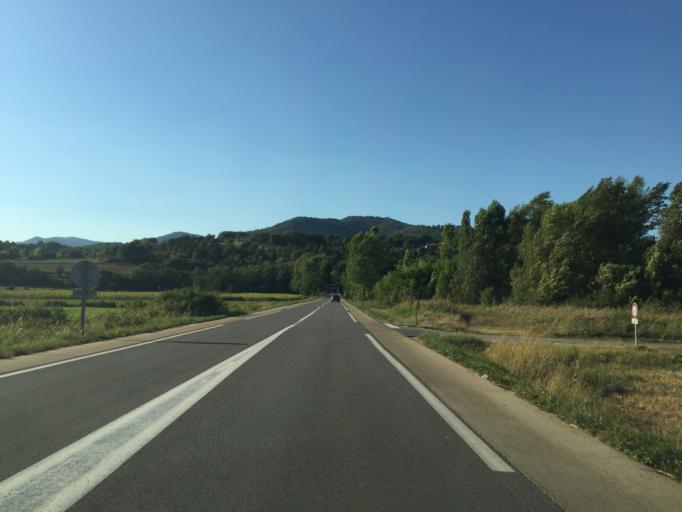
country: FR
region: Provence-Alpes-Cote d'Azur
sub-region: Departement des Alpes-de-Haute-Provence
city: Mallemoisson
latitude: 44.0439
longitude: 6.1391
